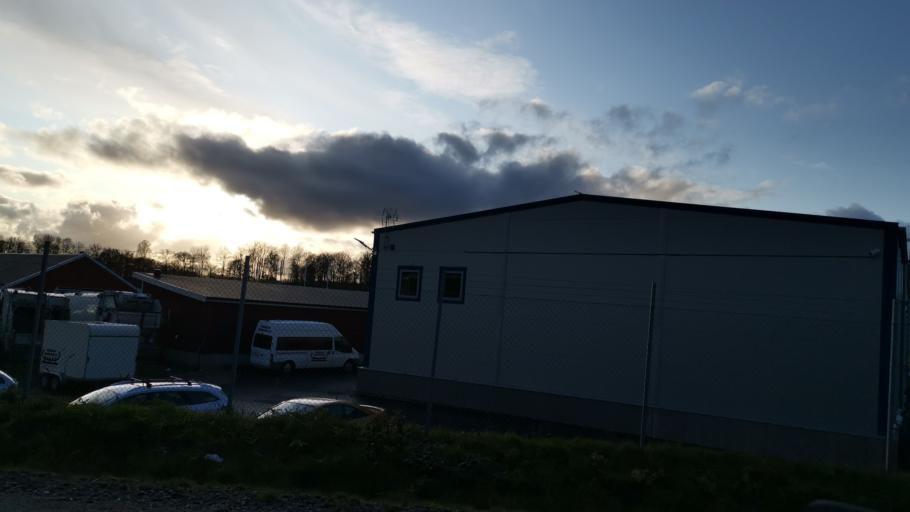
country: SE
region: Vaestra Goetaland
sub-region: Munkedals Kommun
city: Munkedal
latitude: 58.4605
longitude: 11.6598
